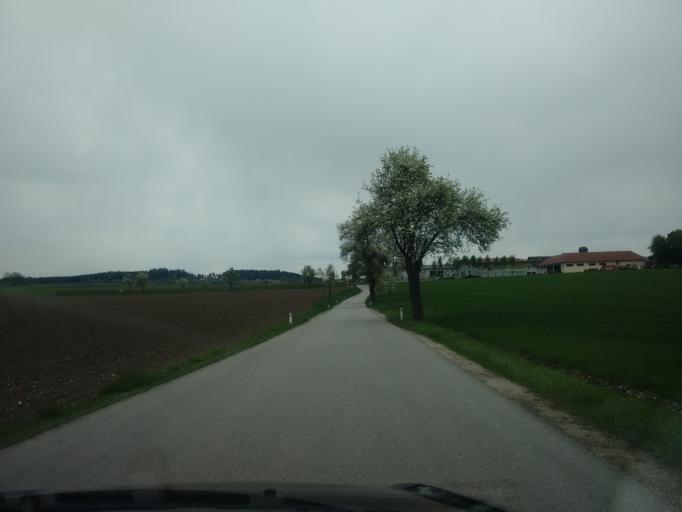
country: AT
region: Upper Austria
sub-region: Wels-Land
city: Buchkirchen
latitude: 48.2307
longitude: 14.0572
